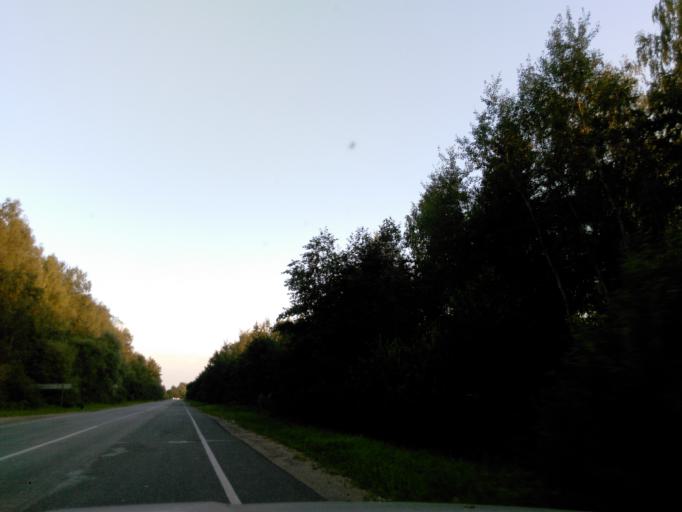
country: RU
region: Tverskaya
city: Konakovo
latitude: 56.6492
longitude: 36.7085
